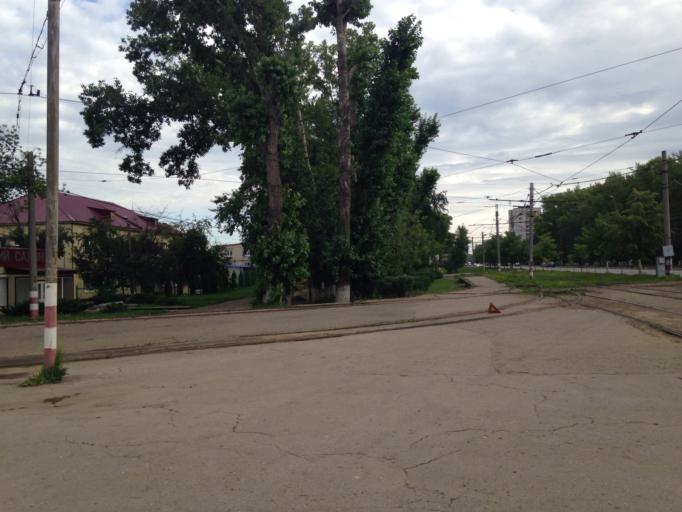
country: RU
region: Ulyanovsk
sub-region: Ulyanovskiy Rayon
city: Ulyanovsk
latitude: 54.2549
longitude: 48.3188
